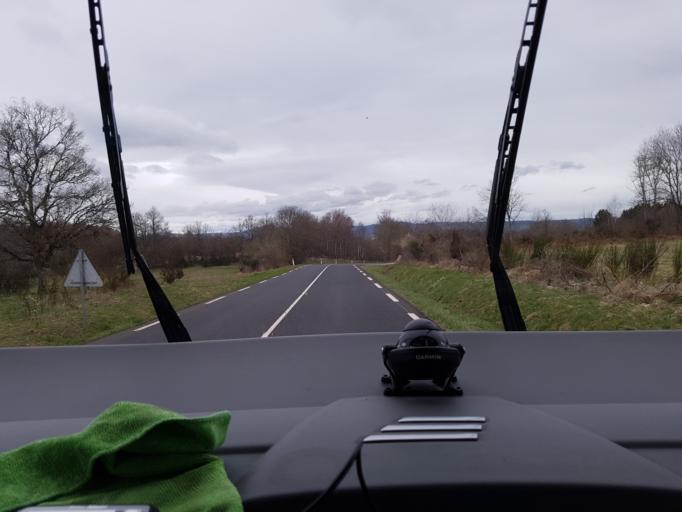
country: FR
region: Auvergne
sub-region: Departement du Puy-de-Dome
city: Saint-Ours
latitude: 45.8564
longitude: 2.9079
